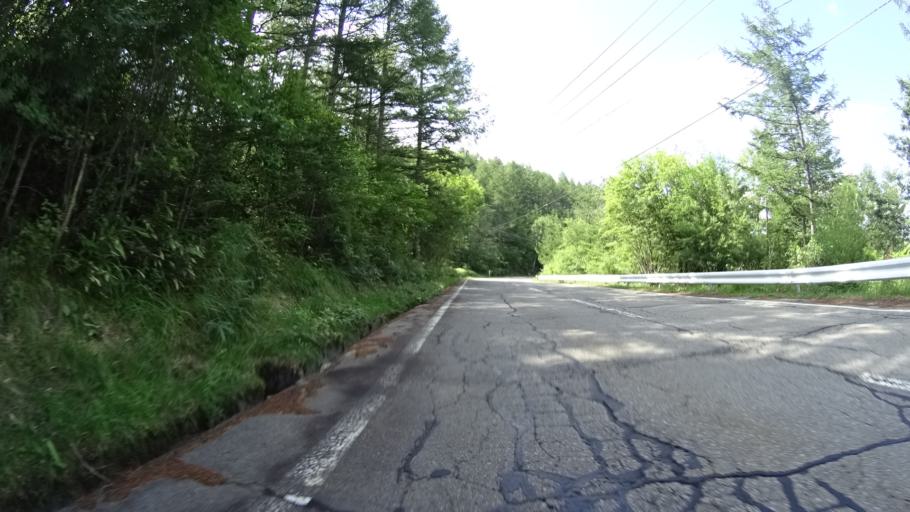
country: JP
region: Nagano
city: Saku
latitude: 36.0576
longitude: 138.3959
